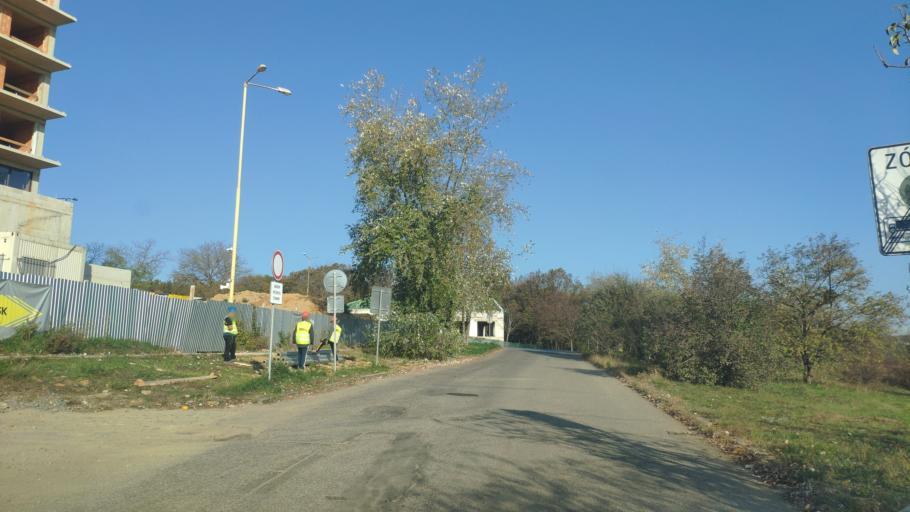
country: SK
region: Kosicky
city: Kosice
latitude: 48.7203
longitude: 21.2173
